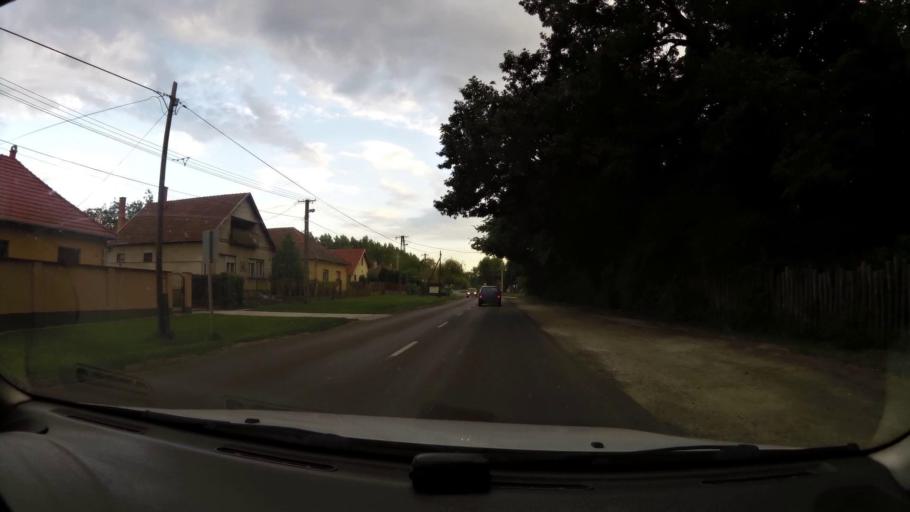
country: HU
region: Pest
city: Tapioszele
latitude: 47.3169
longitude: 19.8743
